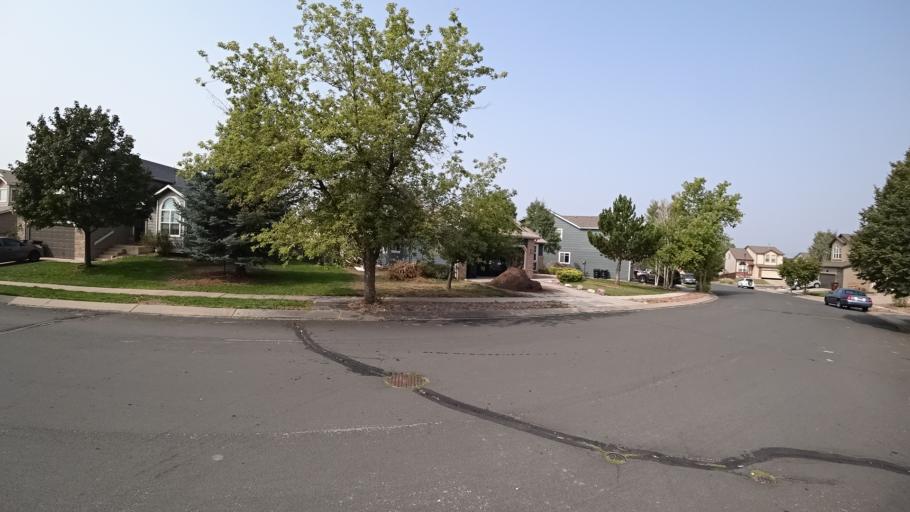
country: US
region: Colorado
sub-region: El Paso County
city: Cimarron Hills
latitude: 38.9266
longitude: -104.7342
